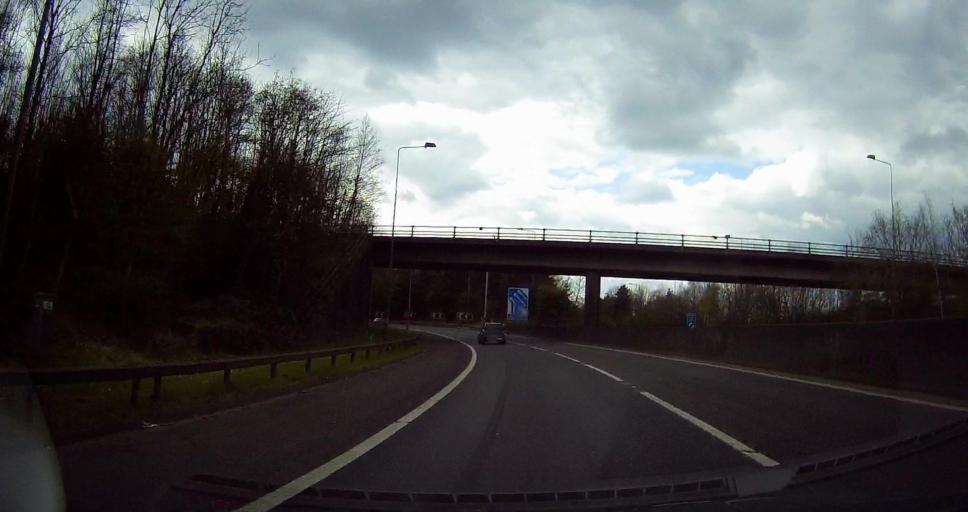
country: GB
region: England
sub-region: Surrey
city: Bletchingley
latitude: 51.2621
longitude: -0.1208
